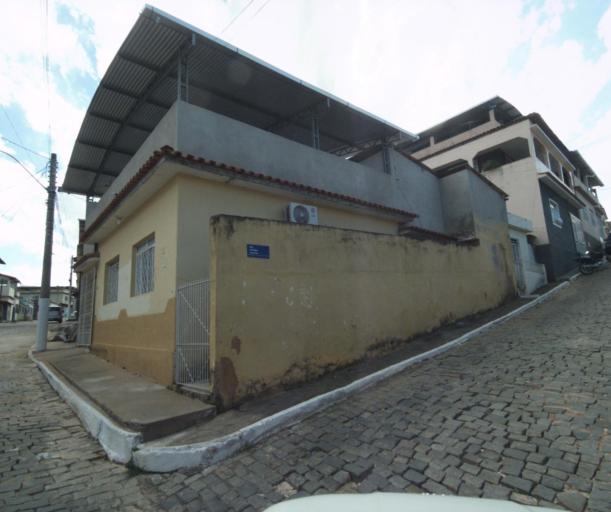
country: BR
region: Espirito Santo
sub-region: Sao Jose Do Calcado
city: Sao Jose do Calcado
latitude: -21.0292
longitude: -41.6560
